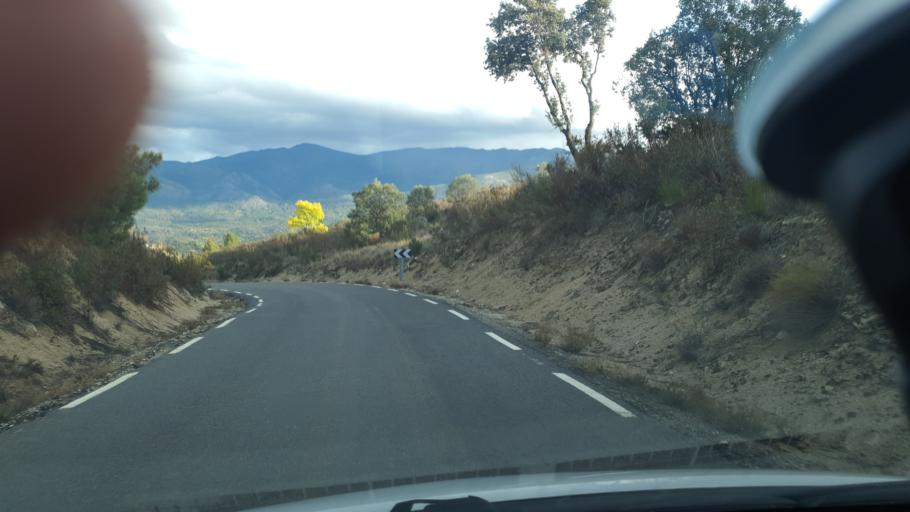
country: ES
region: Castille and Leon
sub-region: Provincia de Avila
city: Burgohondo
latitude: 40.4107
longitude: -4.8254
